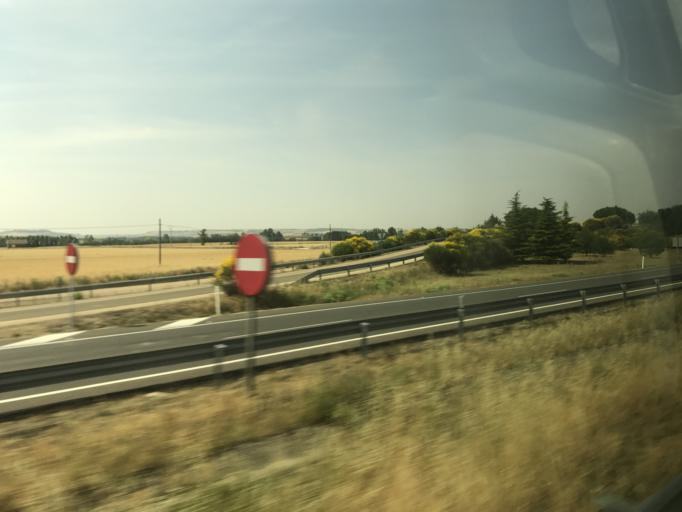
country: ES
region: Castille and Leon
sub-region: Provincia de Palencia
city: Palenzuela
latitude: 42.1209
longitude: -4.1490
